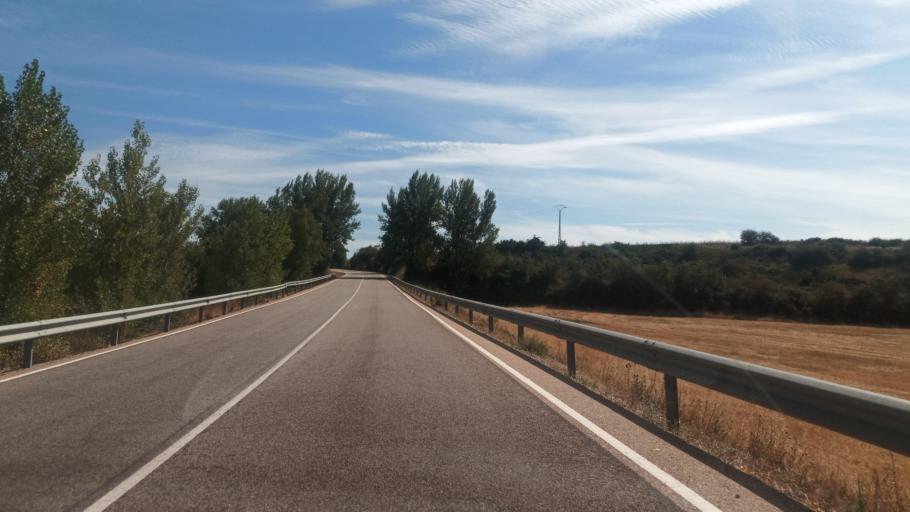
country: ES
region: Castille and Leon
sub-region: Provincia de Burgos
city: Piernigas
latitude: 42.6407
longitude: -3.3868
